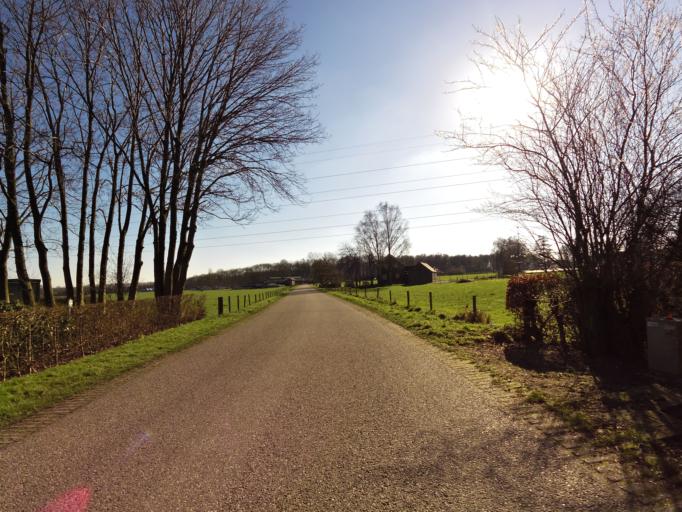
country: NL
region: Gelderland
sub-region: Gemeente Doesburg
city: Doesburg
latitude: 51.9374
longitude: 6.1607
